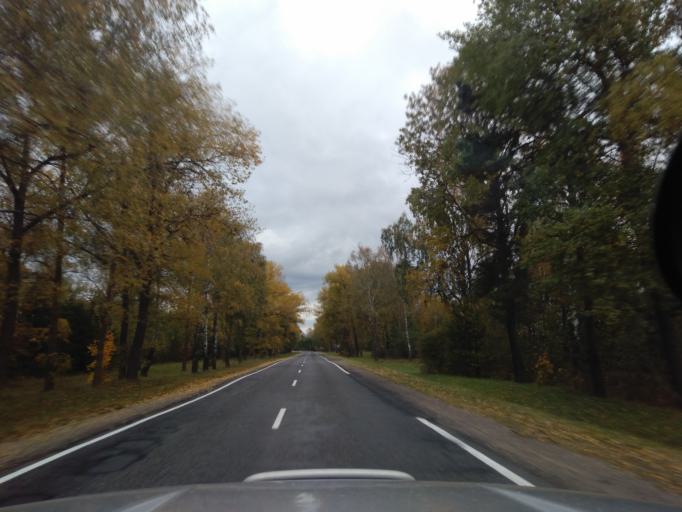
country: BY
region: Minsk
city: Slutsk
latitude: 53.2197
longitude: 27.5235
